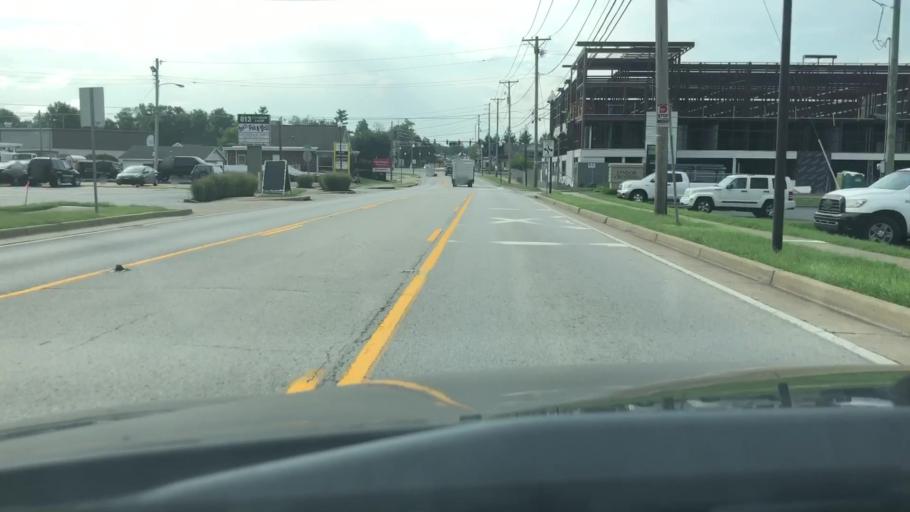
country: US
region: Kentucky
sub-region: Jefferson County
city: Lyndon
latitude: 38.2632
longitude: -85.6081
